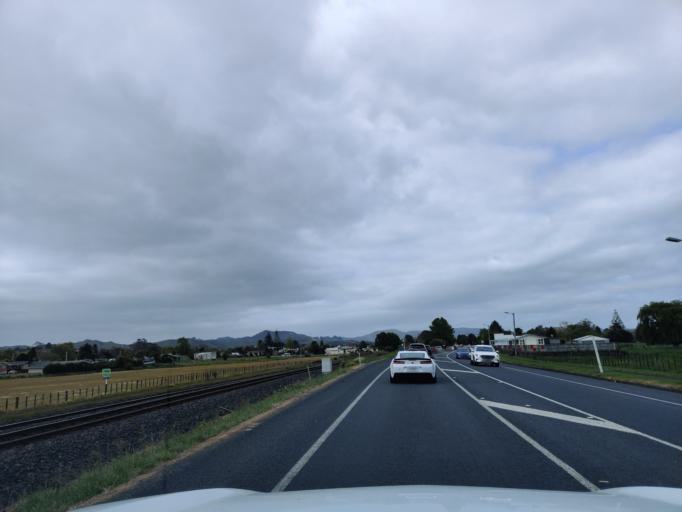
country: NZ
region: Waikato
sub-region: Waikato District
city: Ngaruawahia
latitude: -37.5336
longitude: 175.1593
